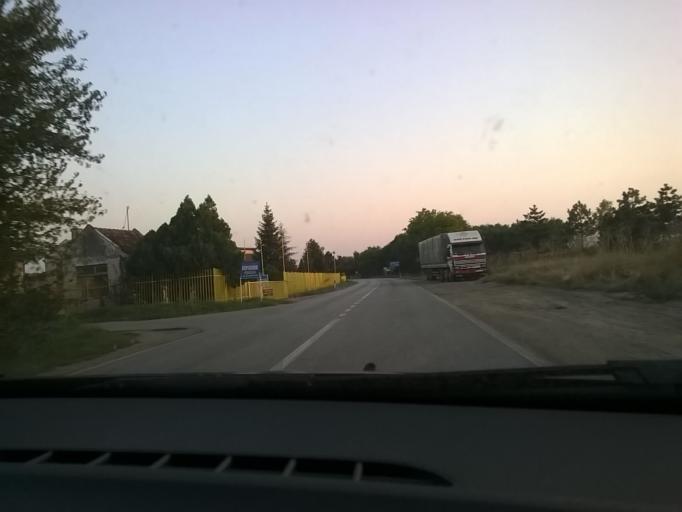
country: RS
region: Autonomna Pokrajina Vojvodina
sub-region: Juznobanatski Okrug
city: Vrsac
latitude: 45.1041
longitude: 21.2982
